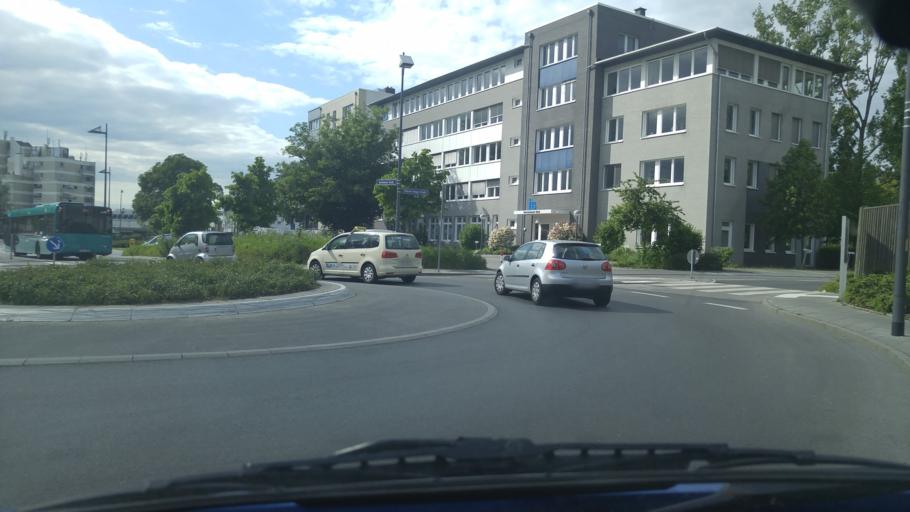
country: DE
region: Hesse
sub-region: Regierungsbezirk Darmstadt
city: Frankfurt am Main
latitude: 50.1387
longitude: 8.7001
